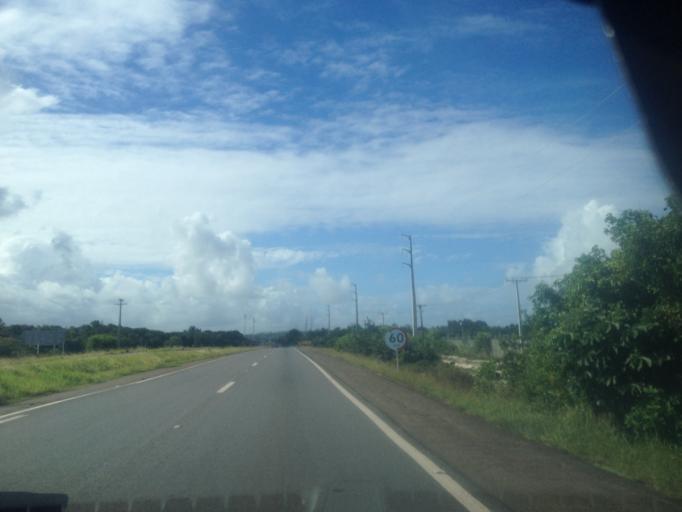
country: BR
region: Bahia
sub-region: Mata De Sao Joao
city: Mata de Sao Joao
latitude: -12.6154
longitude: -38.0550
